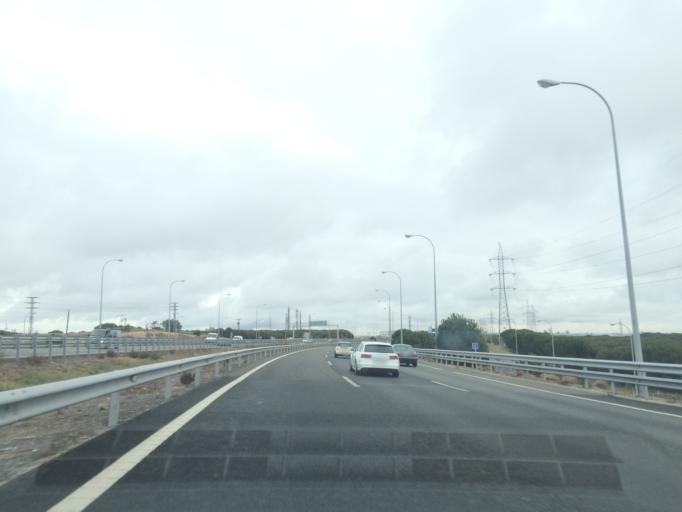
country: ES
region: Madrid
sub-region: Provincia de Madrid
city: Pozuelo de Alarcon
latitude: 40.4063
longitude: -3.8284
